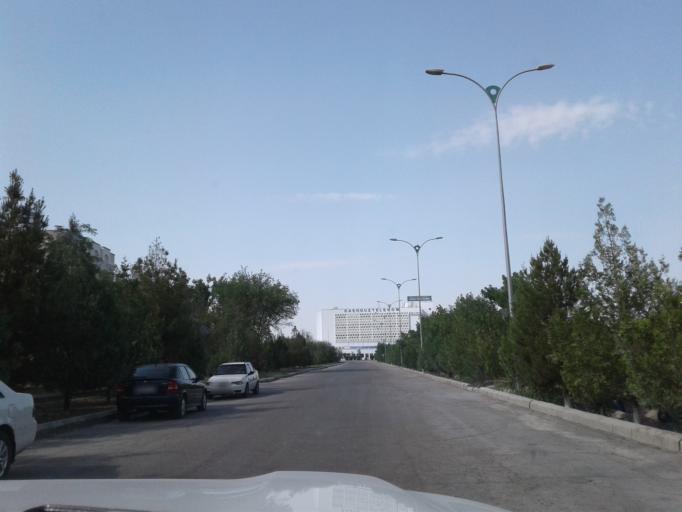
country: TM
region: Dasoguz
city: Dasoguz
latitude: 41.8323
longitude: 59.9641
